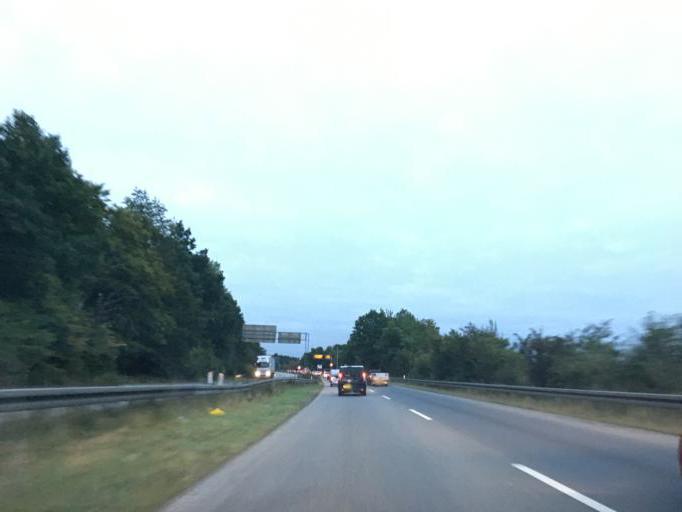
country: DK
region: Capital Region
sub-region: Horsholm Kommune
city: Horsholm
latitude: 55.8694
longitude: 12.4829
